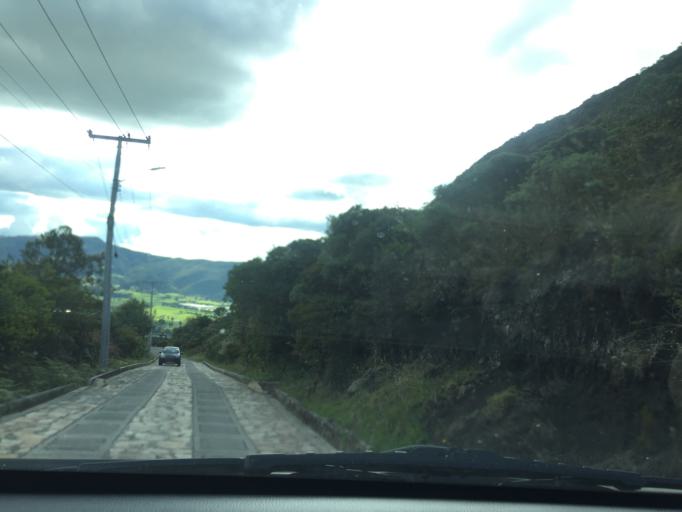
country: CO
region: Cundinamarca
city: Sopo
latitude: 4.9155
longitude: -73.9228
